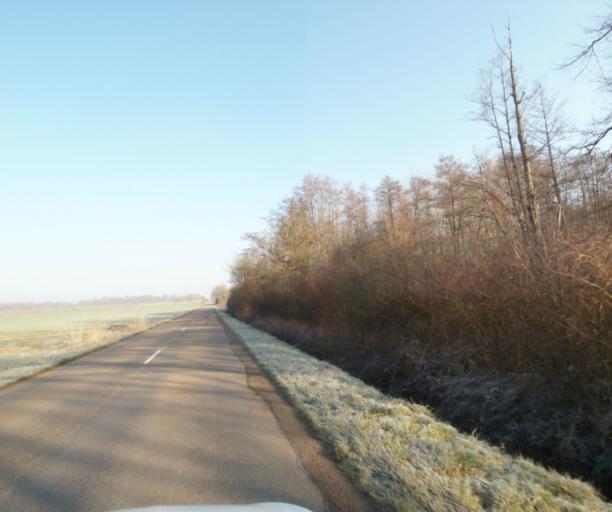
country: FR
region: Champagne-Ardenne
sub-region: Departement de la Haute-Marne
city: Montier-en-Der
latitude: 48.4205
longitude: 4.7451
